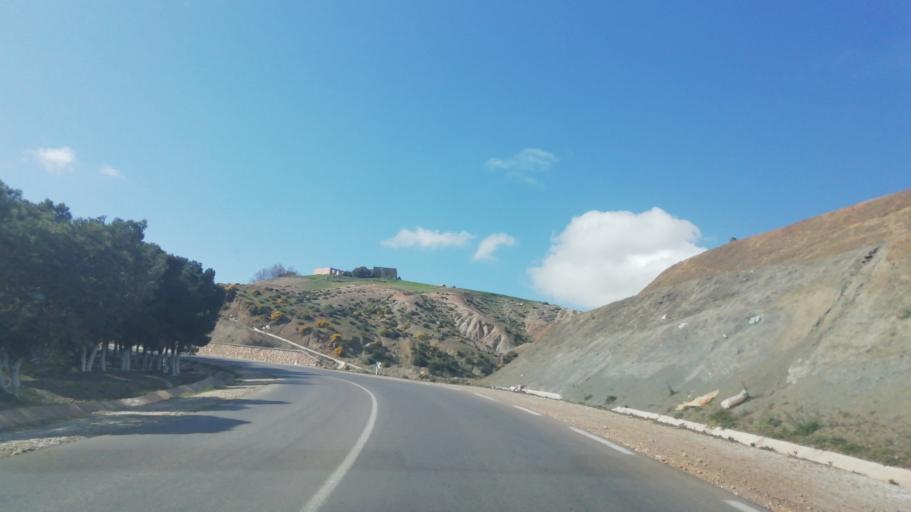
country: DZ
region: Relizane
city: Djidiouia
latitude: 36.0949
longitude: 0.5364
